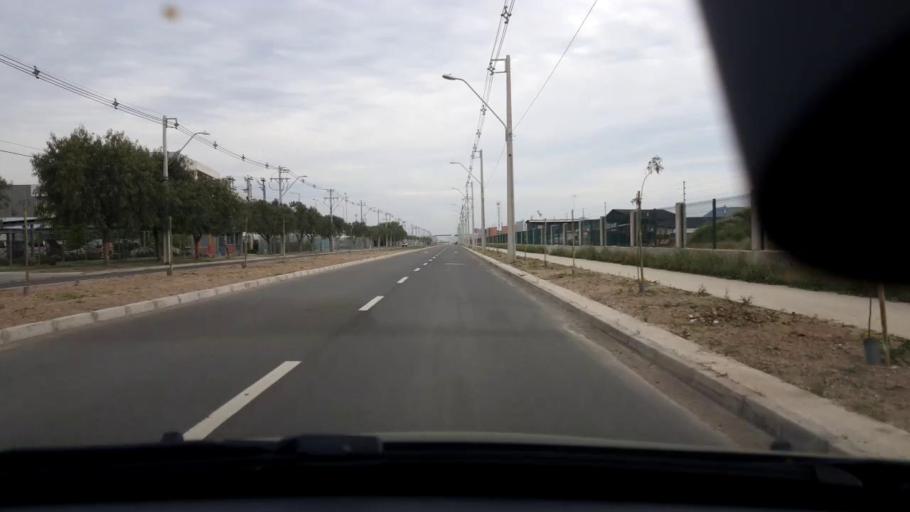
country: CL
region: Santiago Metropolitan
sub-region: Provincia de Santiago
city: Lo Prado
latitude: -33.4266
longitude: -70.7872
